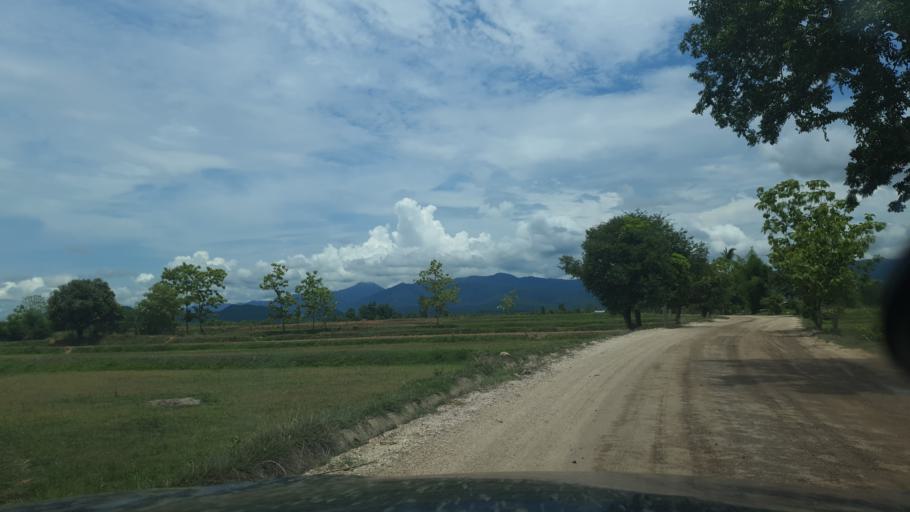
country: TH
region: Lampang
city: Sop Prap
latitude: 17.9390
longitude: 99.3579
